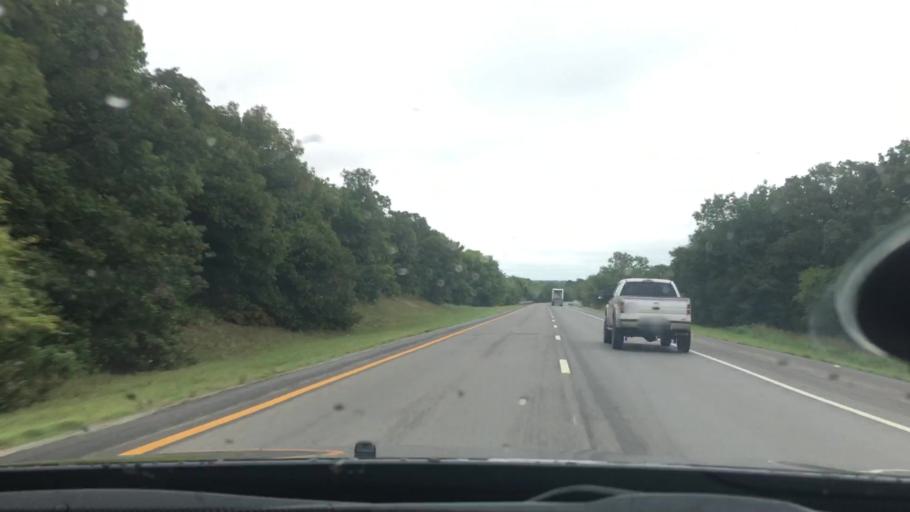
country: US
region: Oklahoma
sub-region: Okmulgee County
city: Morris
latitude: 35.4447
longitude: -95.7706
